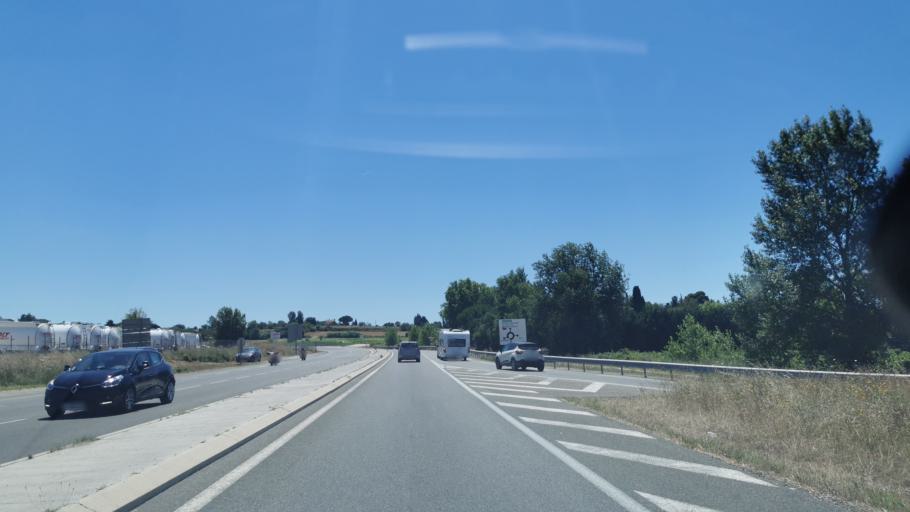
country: FR
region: Languedoc-Roussillon
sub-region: Departement de l'Herault
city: Beziers
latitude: 43.3251
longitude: 3.1906
